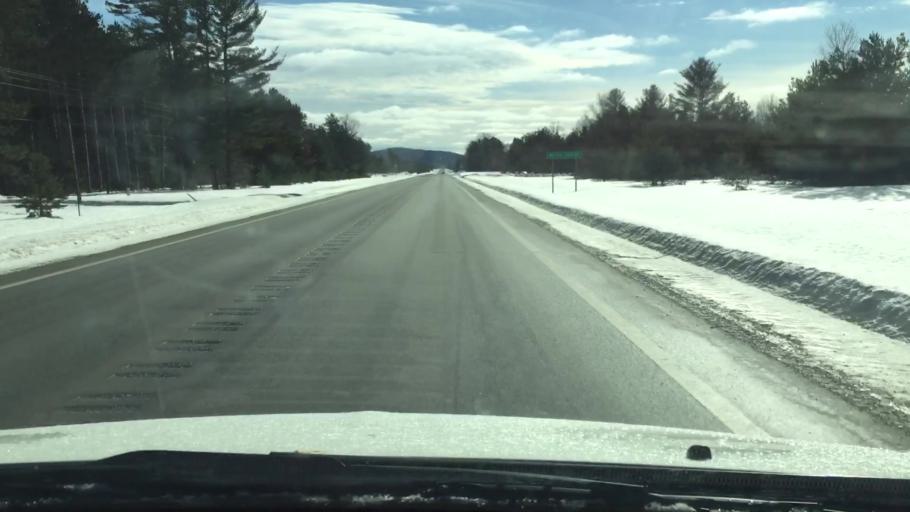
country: US
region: Michigan
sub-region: Antrim County
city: Mancelona
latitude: 44.9337
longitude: -85.0509
